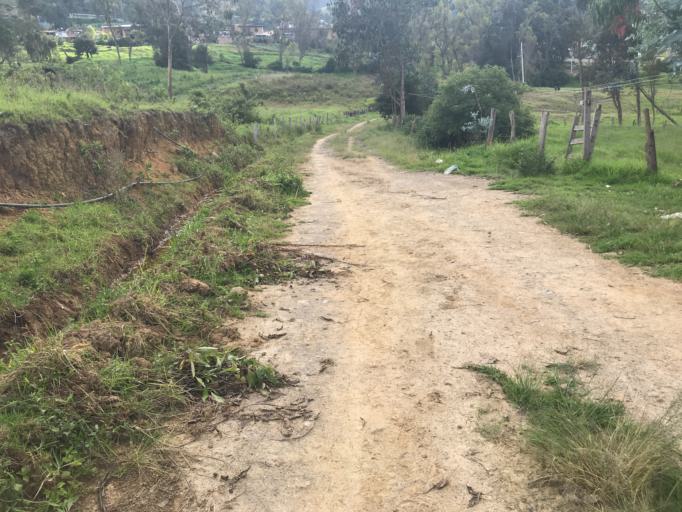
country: PE
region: Cajamarca
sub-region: Provincia de Chota
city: Querocoto
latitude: -6.3589
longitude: -79.0311
